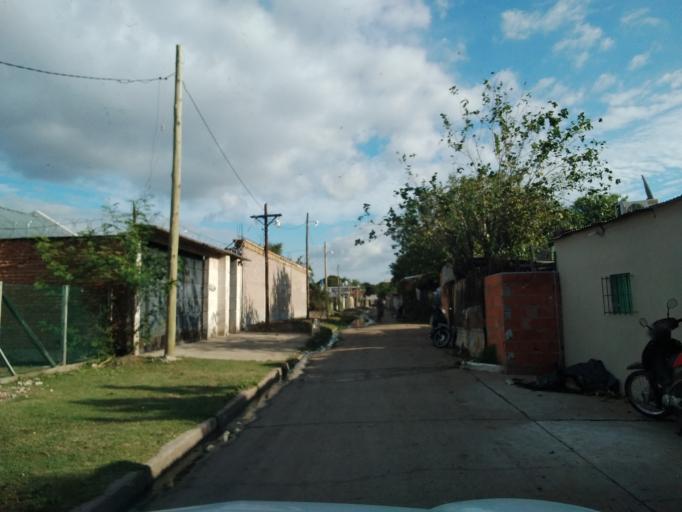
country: AR
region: Corrientes
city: Corrientes
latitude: -27.4599
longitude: -58.8172
